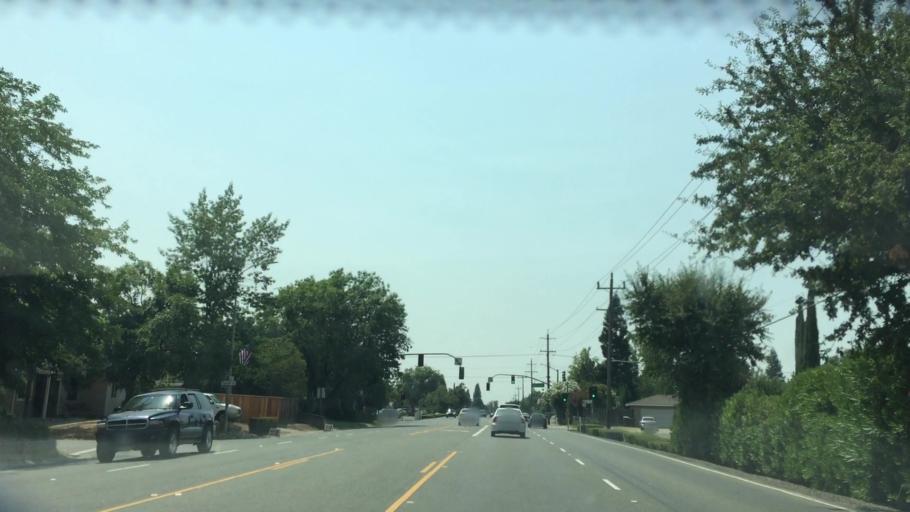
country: US
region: California
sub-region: Sacramento County
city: Arden-Arcade
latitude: 38.6041
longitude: -121.3646
